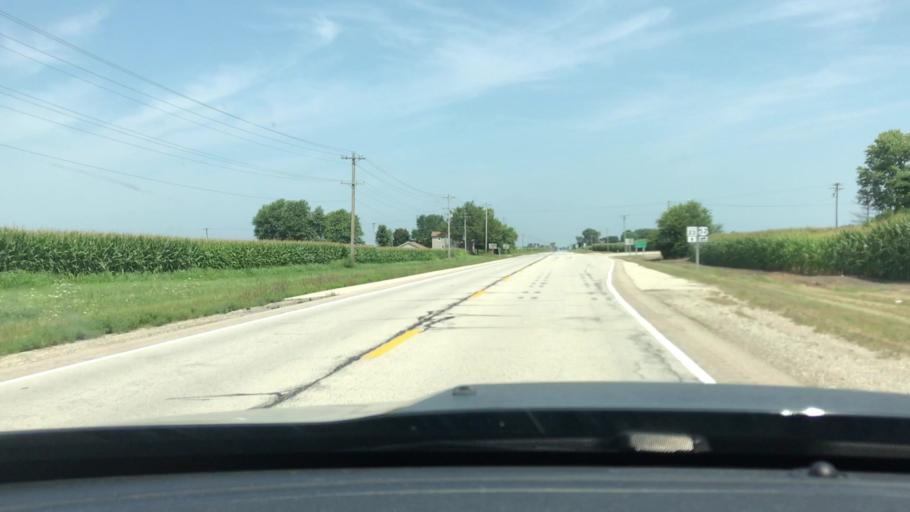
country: US
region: Illinois
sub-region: LaSalle County
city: Ottawa
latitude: 41.4837
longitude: -88.8151
